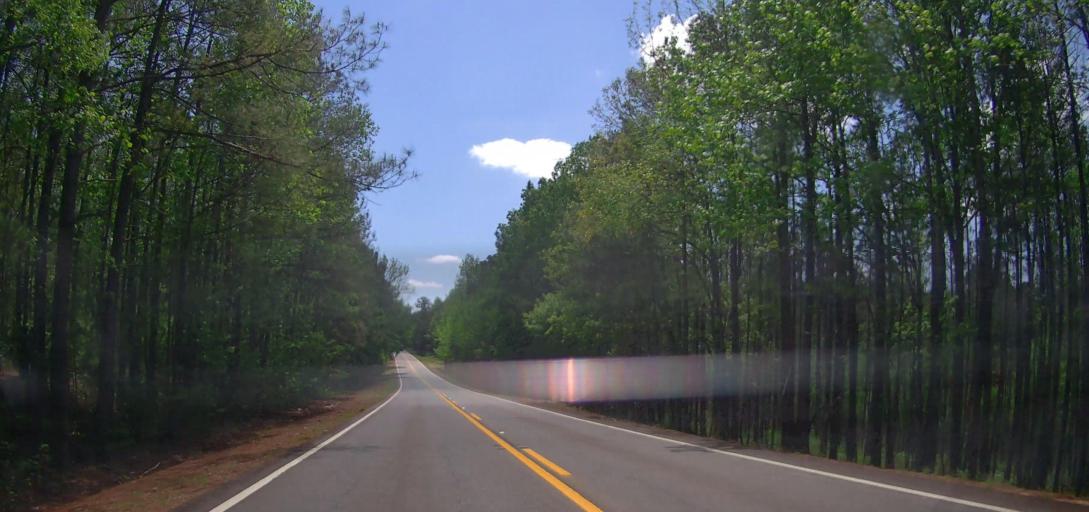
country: US
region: Georgia
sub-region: Jones County
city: Gray
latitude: 33.1250
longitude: -83.6282
